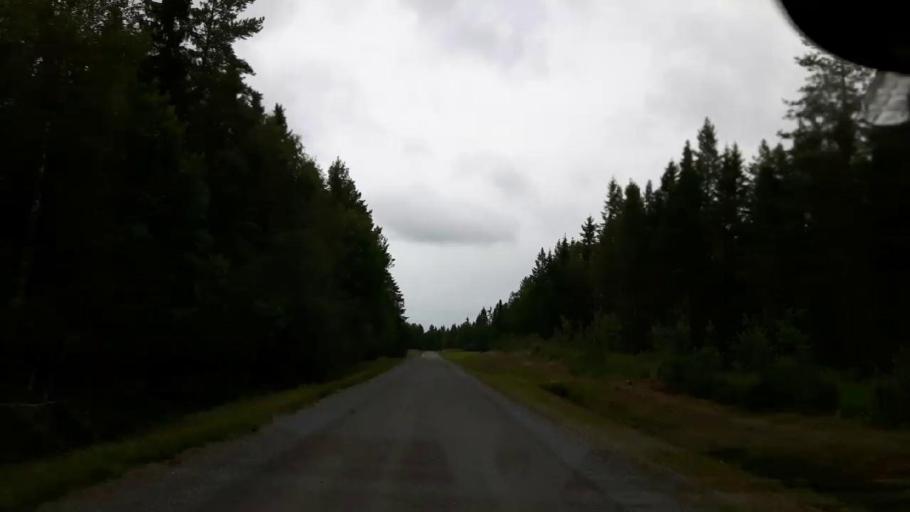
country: SE
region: Jaemtland
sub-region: OEstersunds Kommun
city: Ostersund
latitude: 63.0751
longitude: 14.5540
